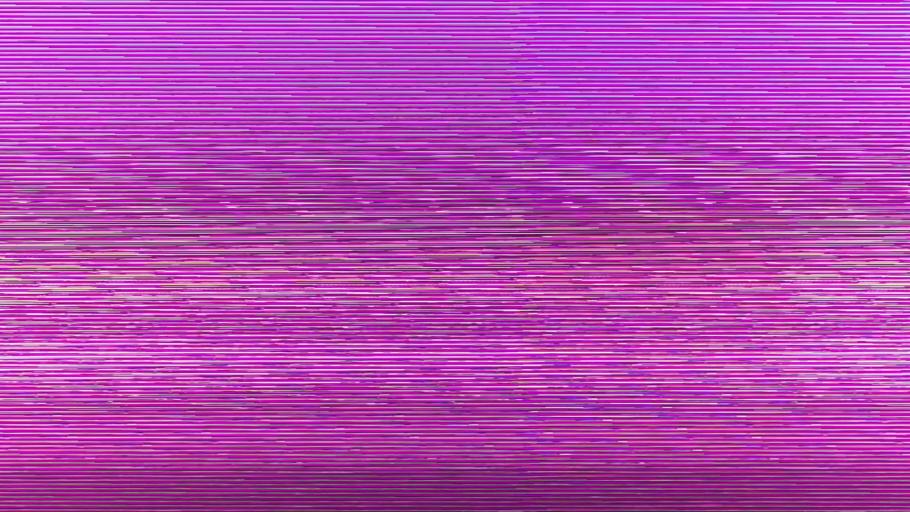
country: US
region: Michigan
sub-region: Genesee County
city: Linden
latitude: 42.8231
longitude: -83.7831
